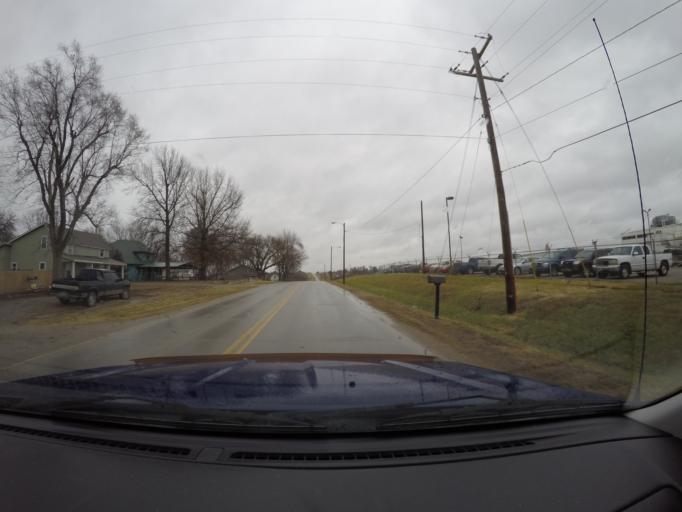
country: US
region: Kansas
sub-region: Jackson County
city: Holton
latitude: 39.4631
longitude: -95.7279
